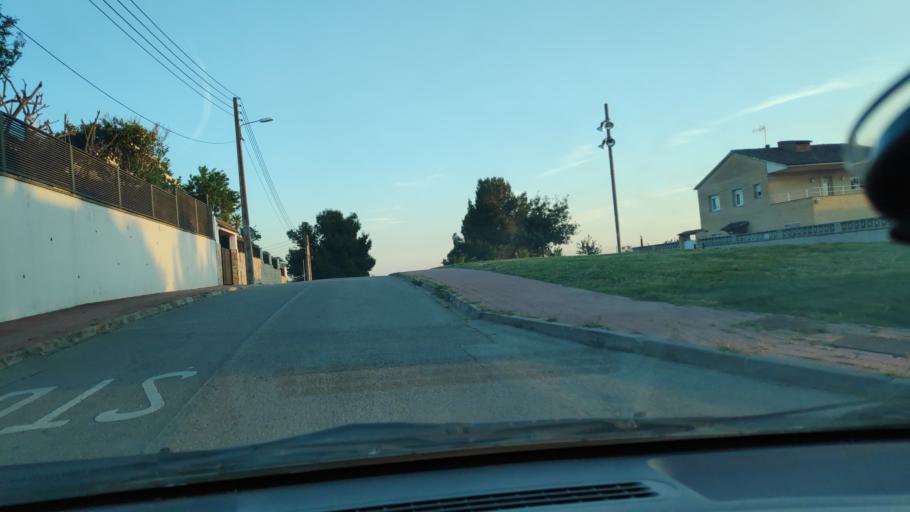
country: ES
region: Catalonia
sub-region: Provincia de Barcelona
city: Sant Quirze del Valles
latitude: 41.5323
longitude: 2.0484
